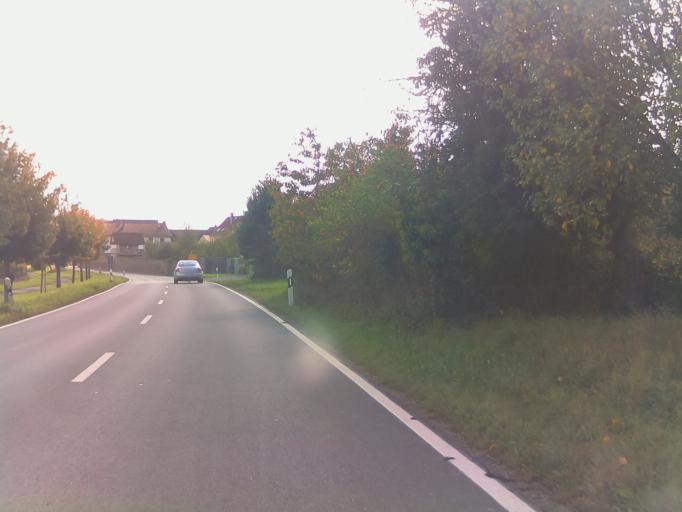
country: DE
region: Bavaria
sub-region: Regierungsbezirk Unterfranken
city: Mainstockheim
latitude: 49.7799
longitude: 10.1512
